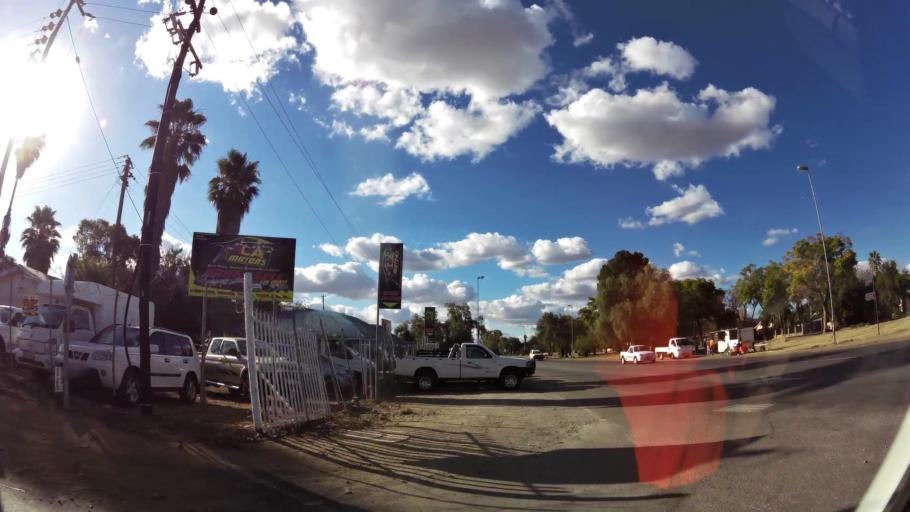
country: ZA
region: Limpopo
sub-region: Capricorn District Municipality
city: Polokwane
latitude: -23.9298
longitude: 29.4504
